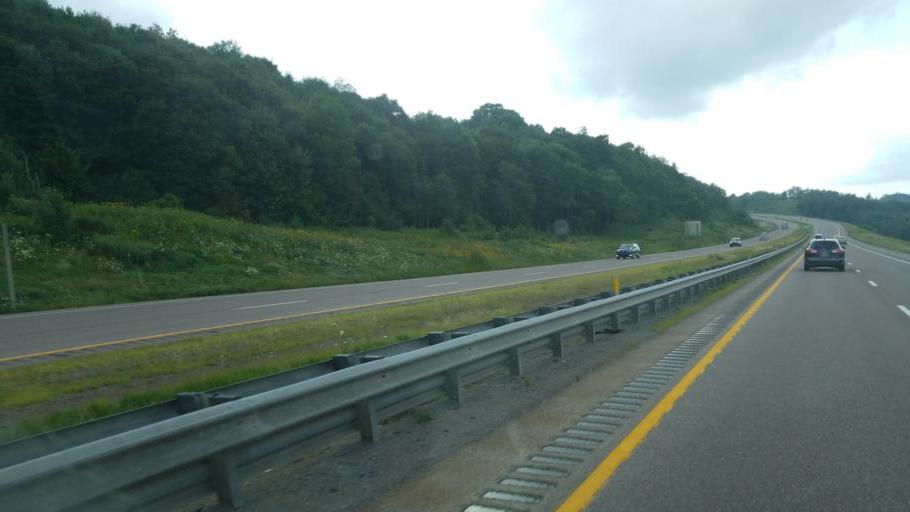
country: US
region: Pennsylvania
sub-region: Somerset County
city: Meyersdale
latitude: 39.6968
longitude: -79.2787
